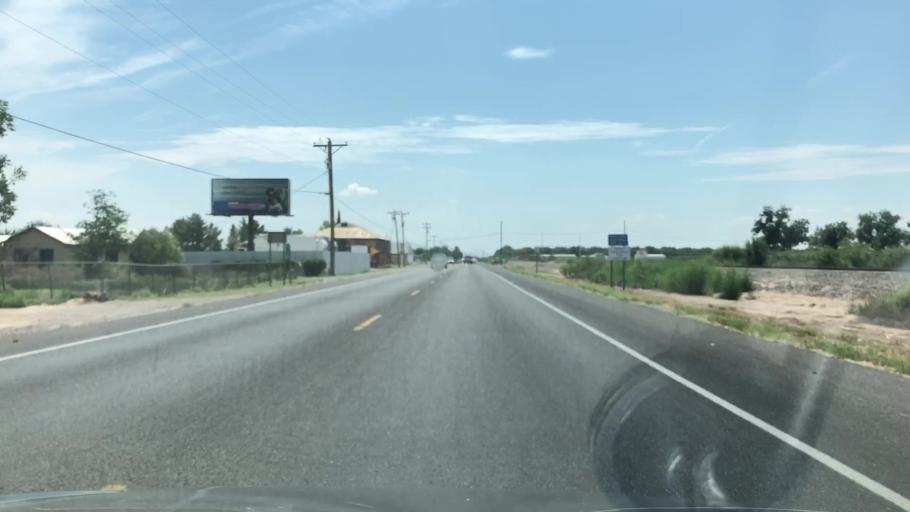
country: US
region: New Mexico
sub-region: Dona Ana County
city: Mesquite
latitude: 32.2107
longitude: -106.7257
